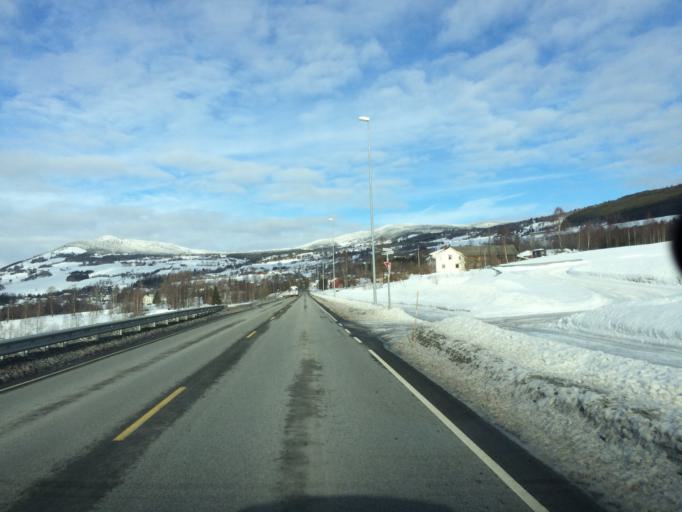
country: NO
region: Oppland
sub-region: Gausdal
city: Segalstad bru
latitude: 61.2043
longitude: 10.3016
